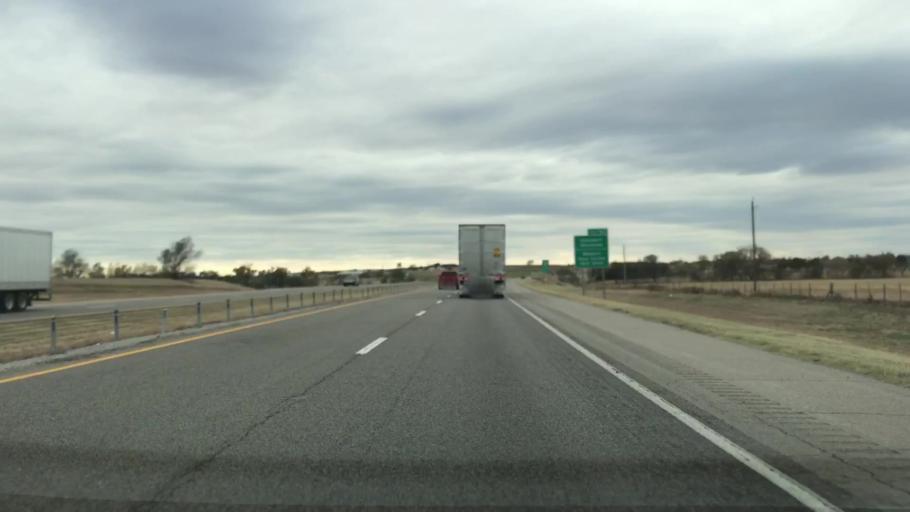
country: US
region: Oklahoma
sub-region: Washita County
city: Burns Flat
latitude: 35.4483
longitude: -99.1627
